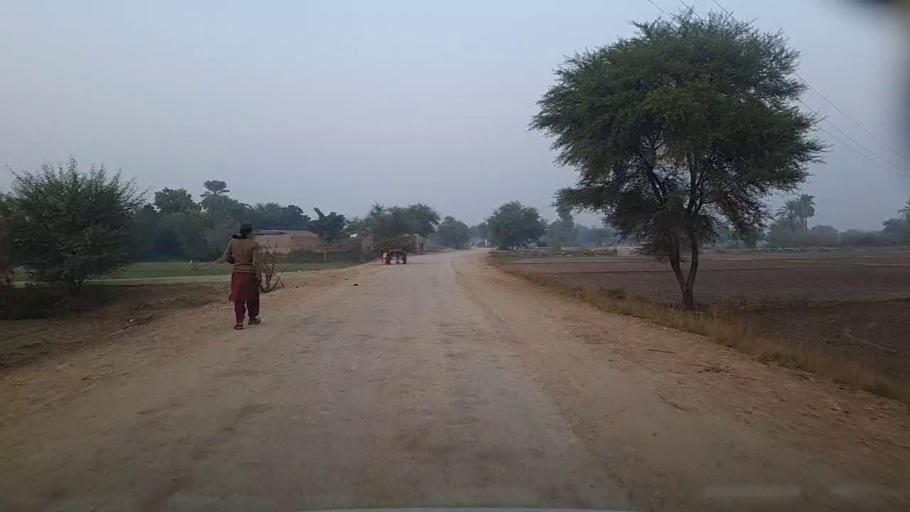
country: PK
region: Sindh
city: Bozdar
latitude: 27.0648
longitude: 68.5964
